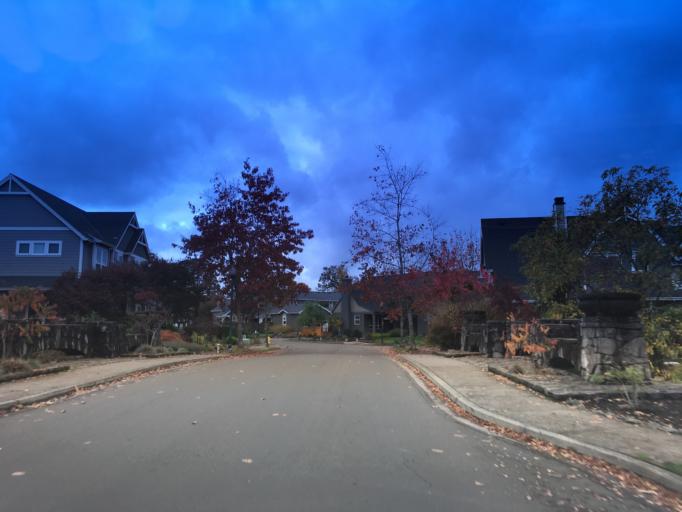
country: US
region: Oregon
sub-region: Multnomah County
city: Fairview
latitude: 45.5308
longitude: -122.4357
